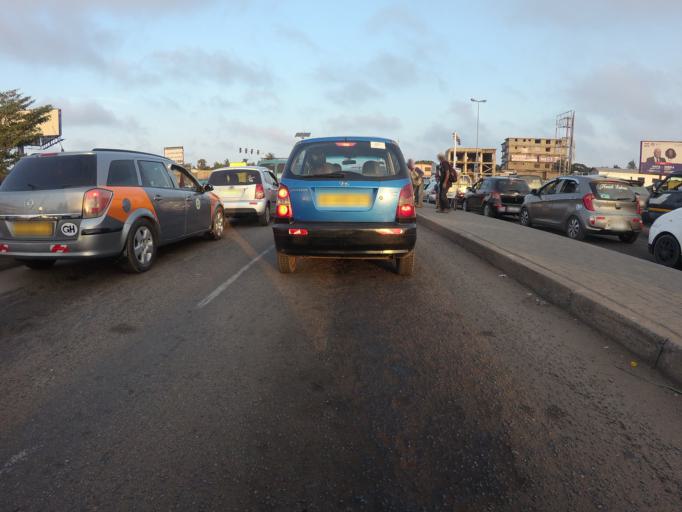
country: GH
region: Greater Accra
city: Gbawe
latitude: 5.5845
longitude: -0.2747
